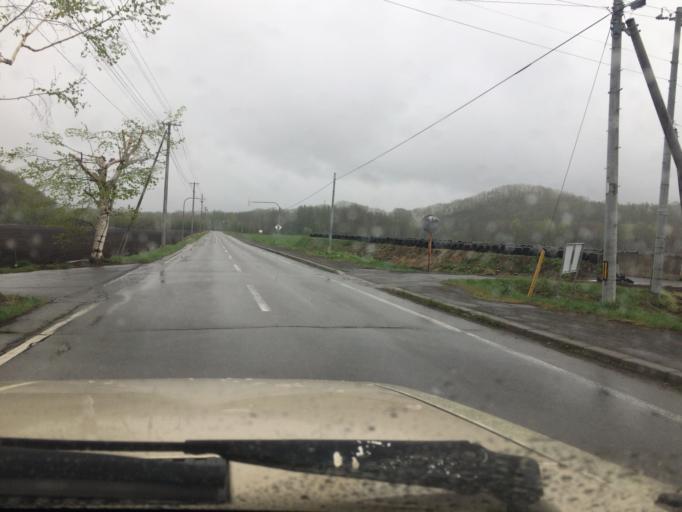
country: JP
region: Hokkaido
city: Obihiro
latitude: 42.8207
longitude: 142.9835
